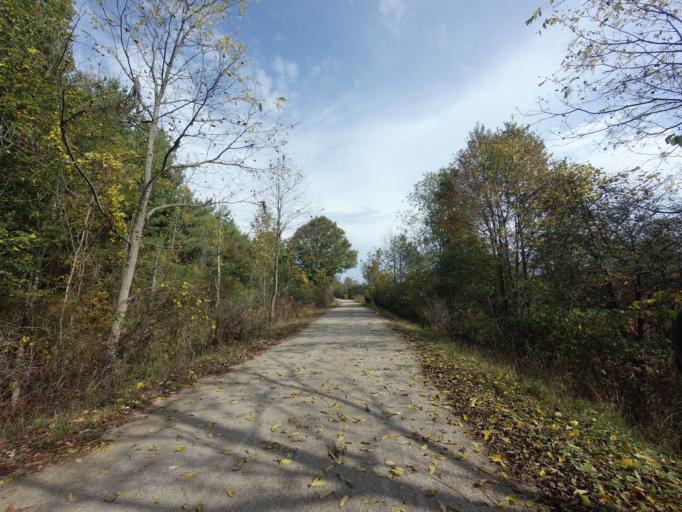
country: CA
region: Ontario
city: Brantford
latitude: 43.1734
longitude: -80.1793
